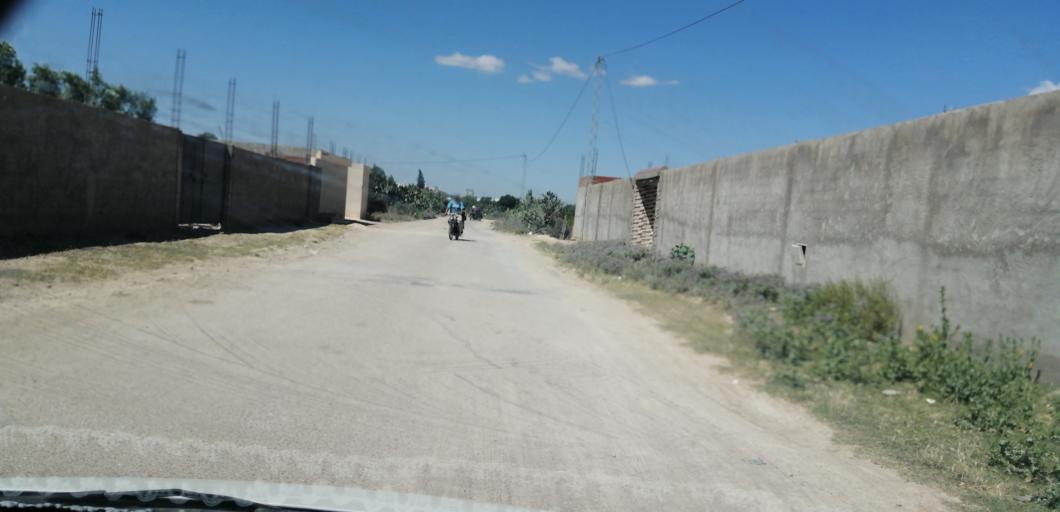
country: TN
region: Al Qayrawan
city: Kairouan
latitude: 35.6254
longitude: 9.9275
